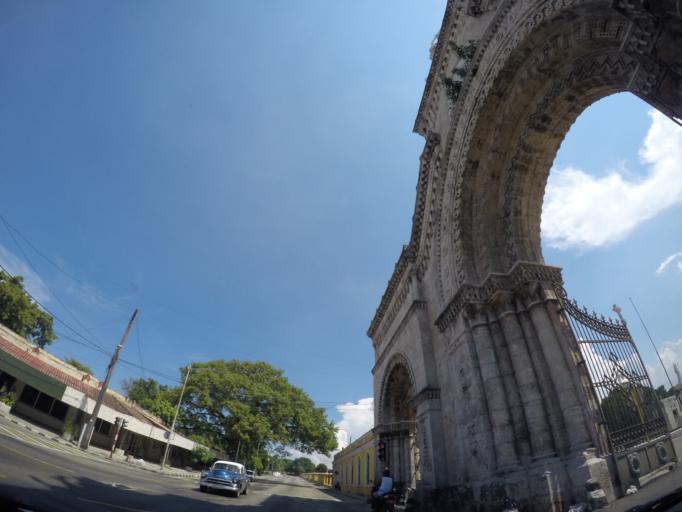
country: CU
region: La Habana
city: Havana
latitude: 23.1259
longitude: -82.3987
